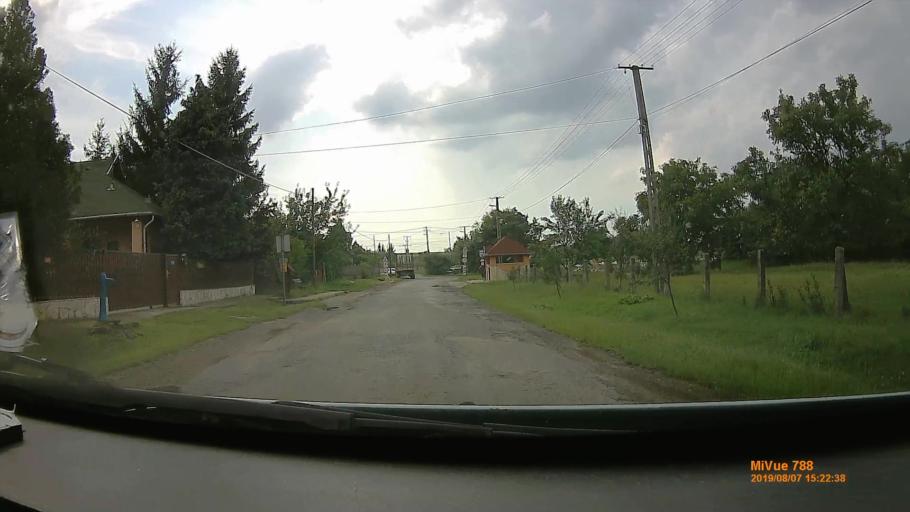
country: HU
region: Borsod-Abauj-Zemplen
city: Encs
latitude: 48.3619
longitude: 21.1418
